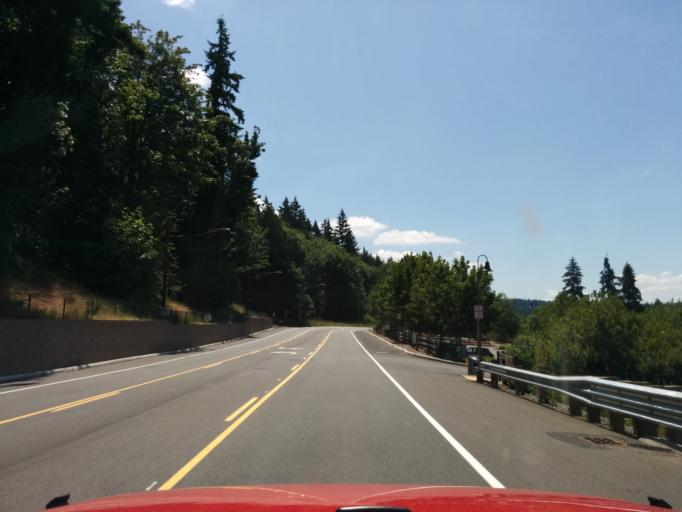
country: US
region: Washington
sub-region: King County
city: Sammamish
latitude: 47.6834
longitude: -122.0798
